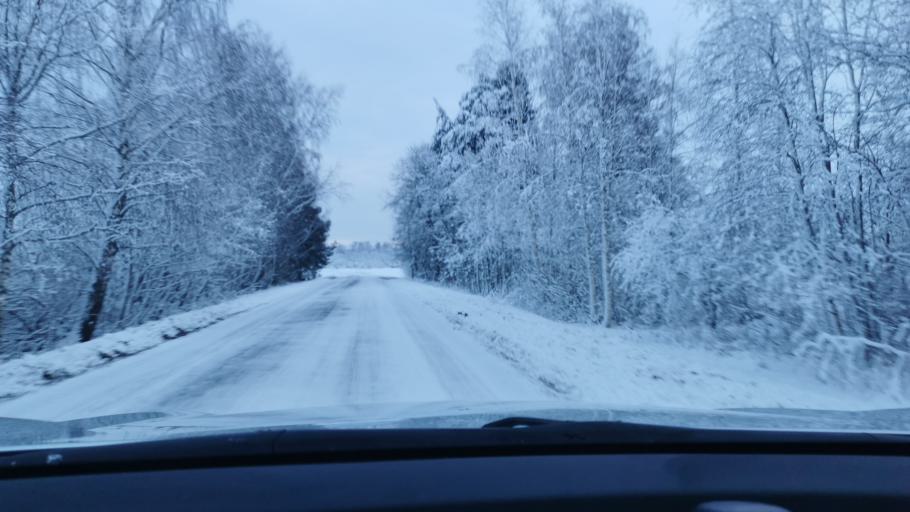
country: EE
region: Laeaene-Virumaa
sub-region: Haljala vald
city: Haljala
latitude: 59.4748
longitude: 26.3609
